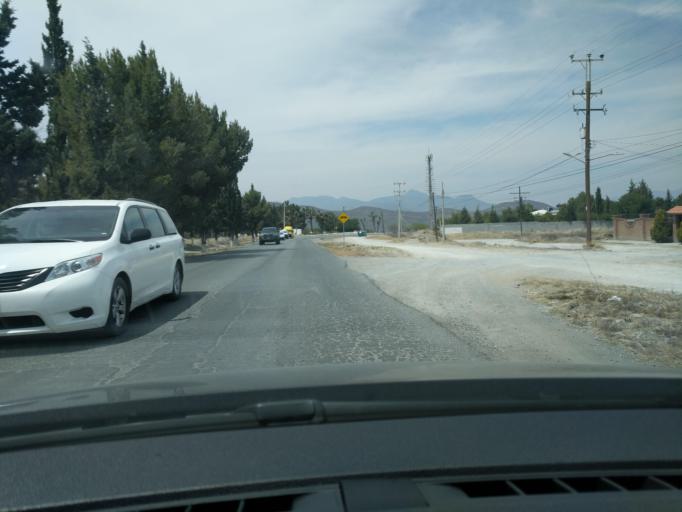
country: MX
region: Coahuila
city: Saltillo
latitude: 25.3558
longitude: -101.0301
